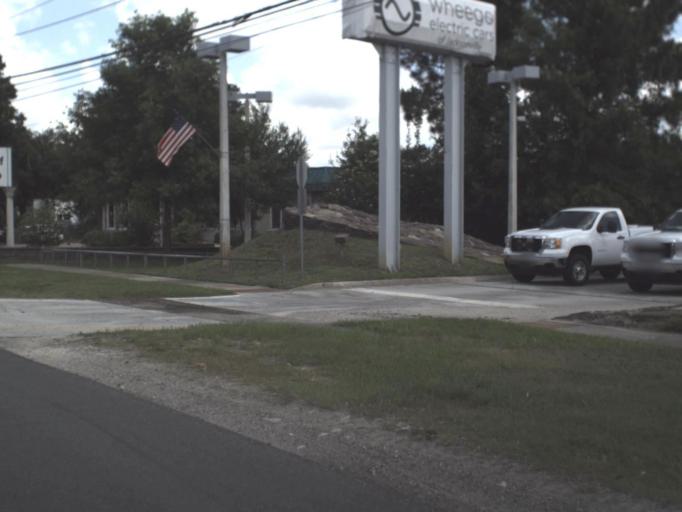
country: US
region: Florida
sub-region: Saint Johns County
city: Fruit Cove
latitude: 30.1616
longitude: -81.5348
